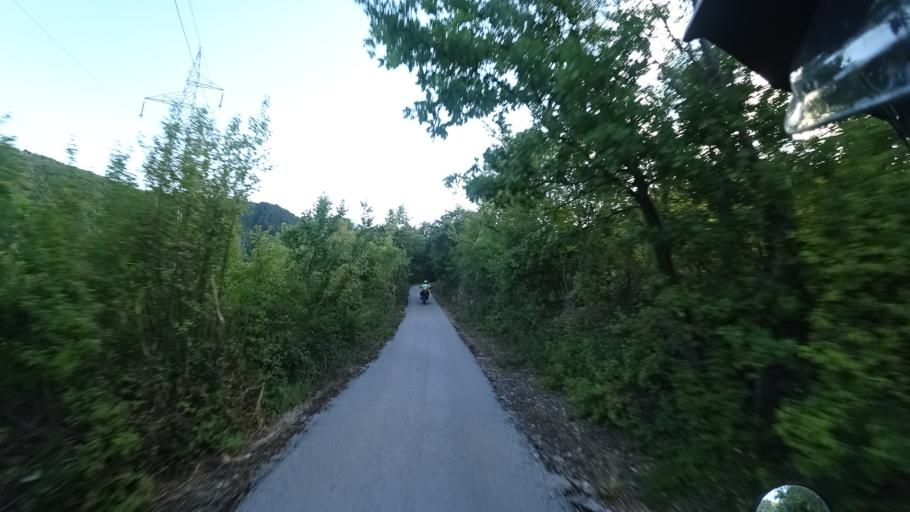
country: HR
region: Sibensko-Kniniska
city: Knin
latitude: 44.2023
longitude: 16.0668
